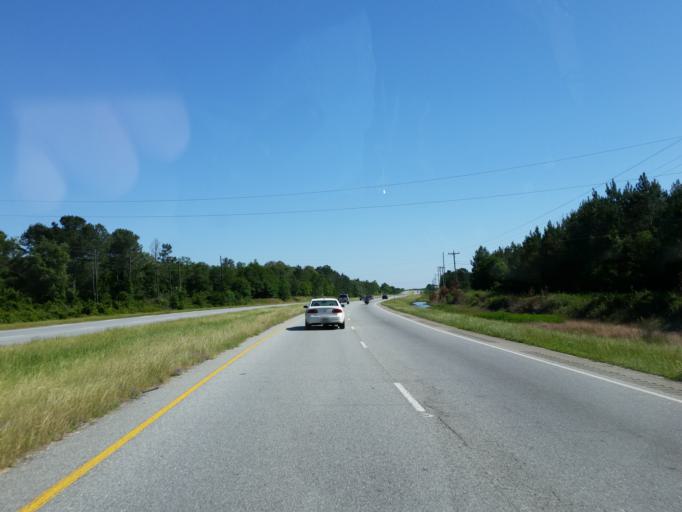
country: US
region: Georgia
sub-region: Lowndes County
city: Valdosta
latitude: 30.8435
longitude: -83.2281
